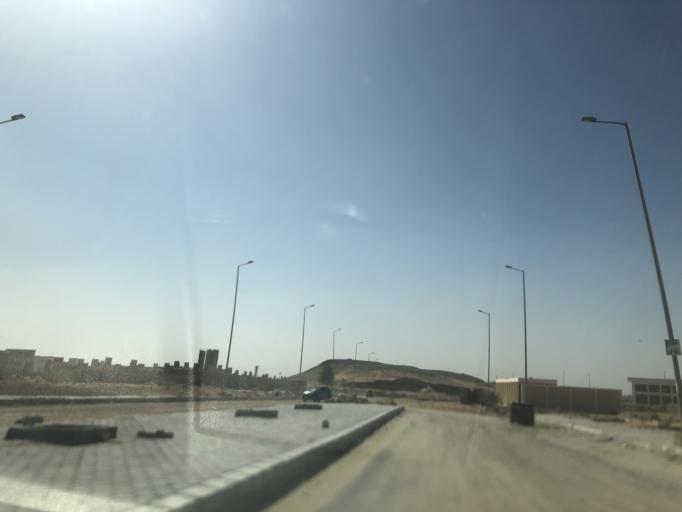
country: EG
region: Al Jizah
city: Madinat Sittah Uktubar
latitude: 29.9330
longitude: 30.9584
